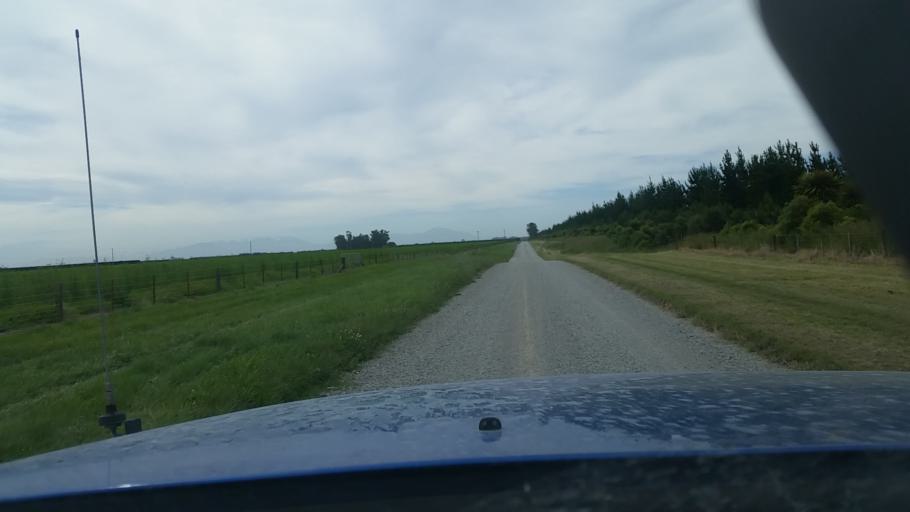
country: NZ
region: Canterbury
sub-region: Ashburton District
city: Tinwald
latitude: -44.0319
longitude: 171.7831
